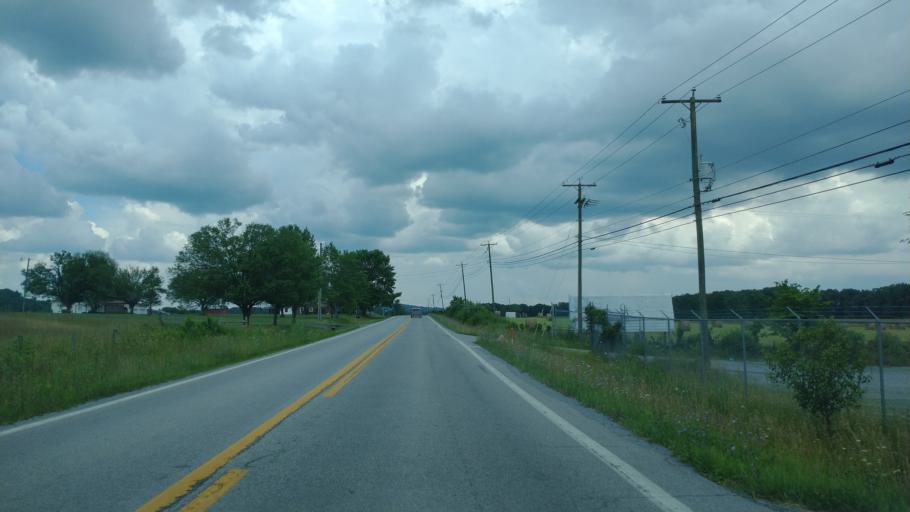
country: US
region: West Virginia
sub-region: Mercer County
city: Athens
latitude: 37.4534
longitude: -81.0087
